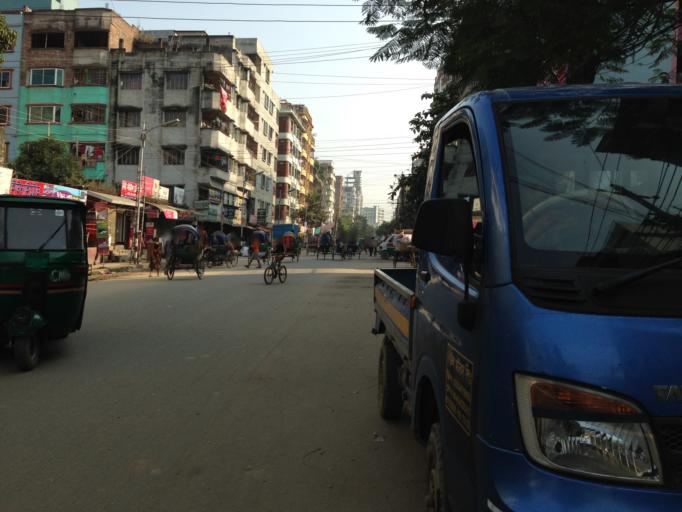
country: BD
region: Dhaka
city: Azimpur
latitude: 23.8016
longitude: 90.3496
